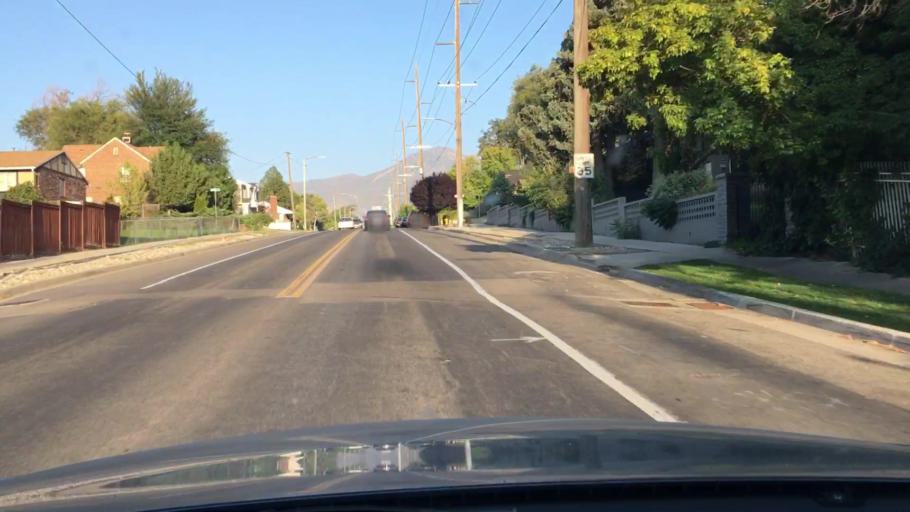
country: US
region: Utah
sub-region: Salt Lake County
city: South Salt Lake
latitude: 40.7126
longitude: -111.8634
